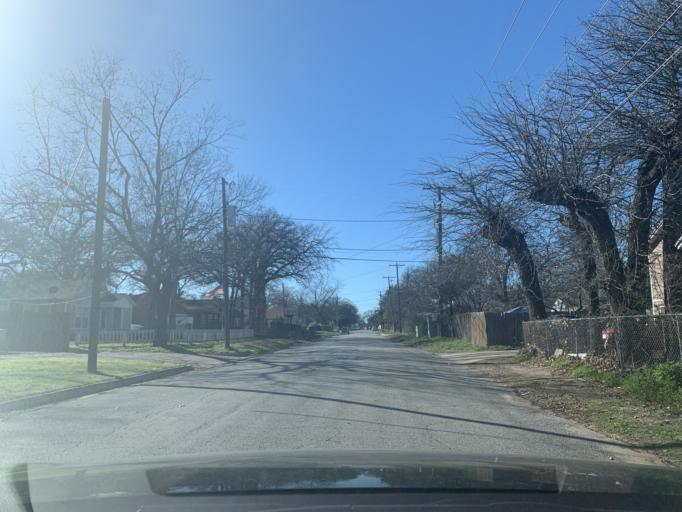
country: US
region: Texas
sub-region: Tarrant County
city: Haltom City
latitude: 32.7796
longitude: -97.2831
